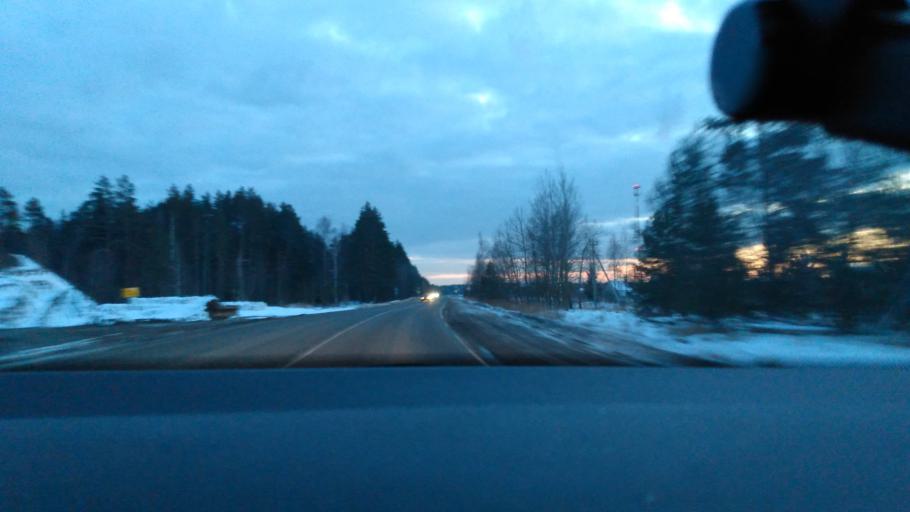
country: RU
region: Moskovskaya
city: Yegor'yevsk
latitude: 55.3422
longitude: 39.0787
